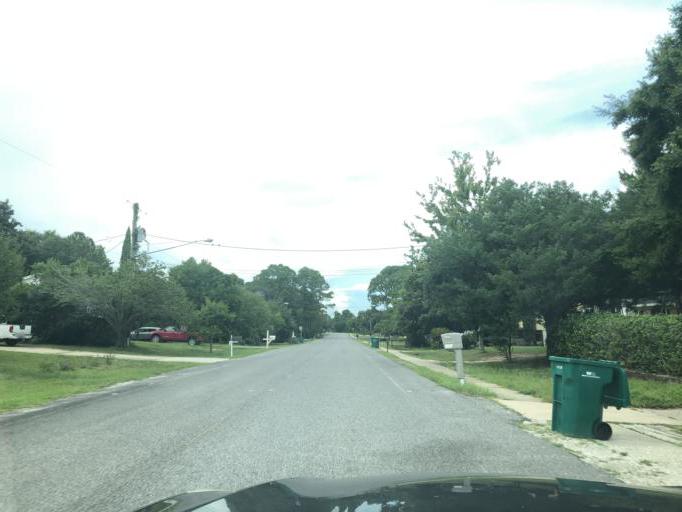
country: US
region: Florida
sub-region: Okaloosa County
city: Destin
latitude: 30.4049
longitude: -86.4952
